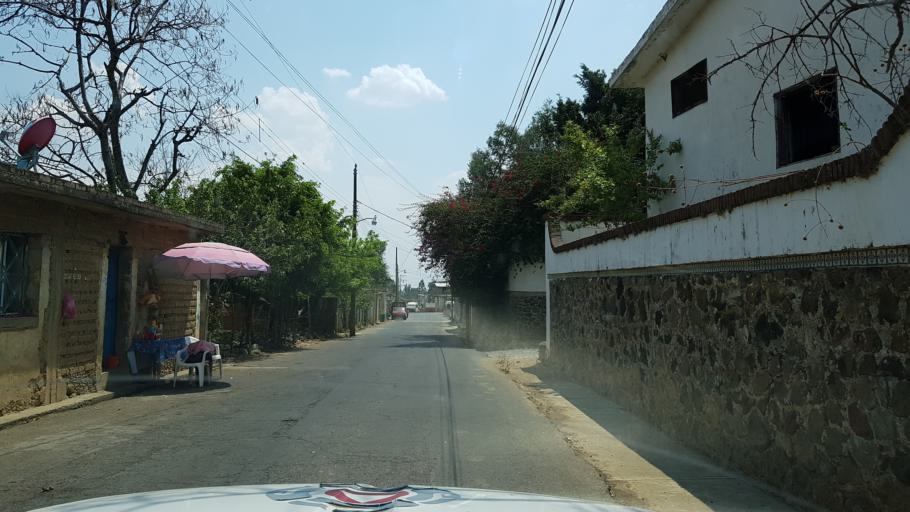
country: MX
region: Morelos
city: Ocuituco
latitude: 18.8894
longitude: -98.8115
